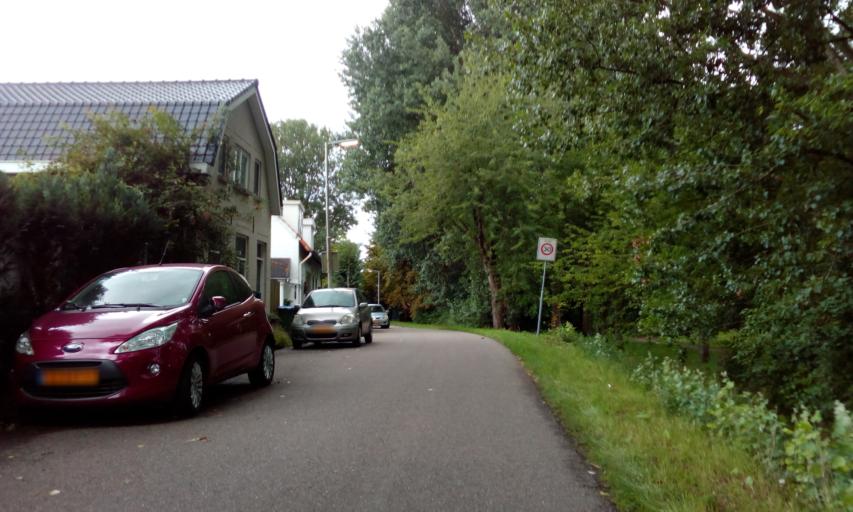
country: NL
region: South Holland
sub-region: Gemeente Barendrecht
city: Barendrecht
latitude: 51.8748
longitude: 4.5507
